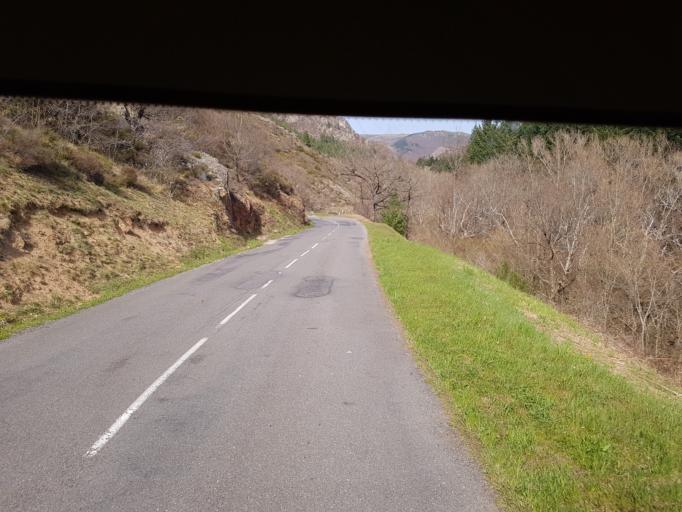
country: FR
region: Languedoc-Roussillon
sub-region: Departement de la Lozere
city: Florac
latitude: 44.3550
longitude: 3.6379
